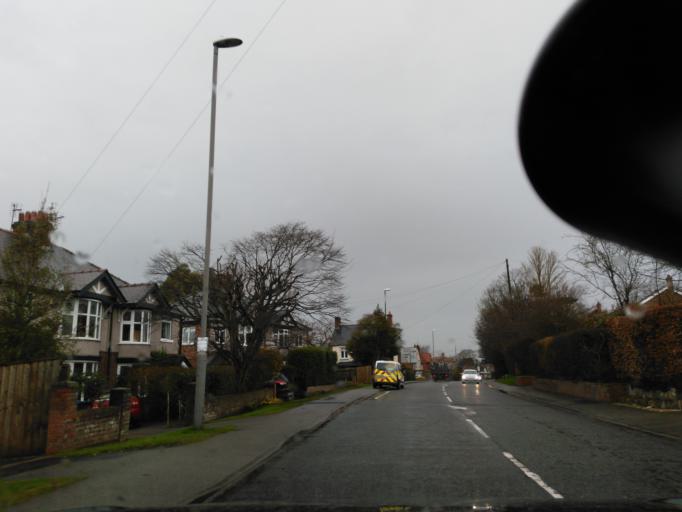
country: GB
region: England
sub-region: North Yorkshire
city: Northallerton
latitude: 54.3308
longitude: -1.4305
